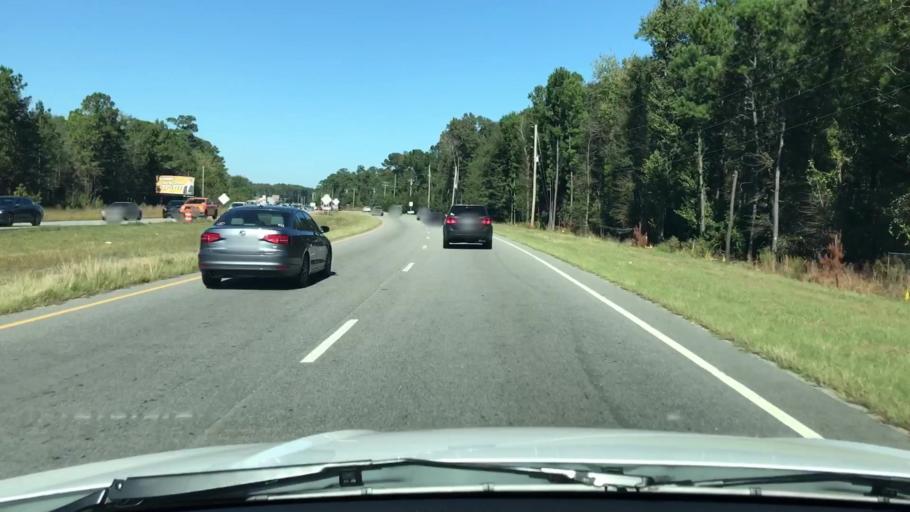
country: US
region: South Carolina
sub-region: Beaufort County
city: Bluffton
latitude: 32.3320
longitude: -80.9283
